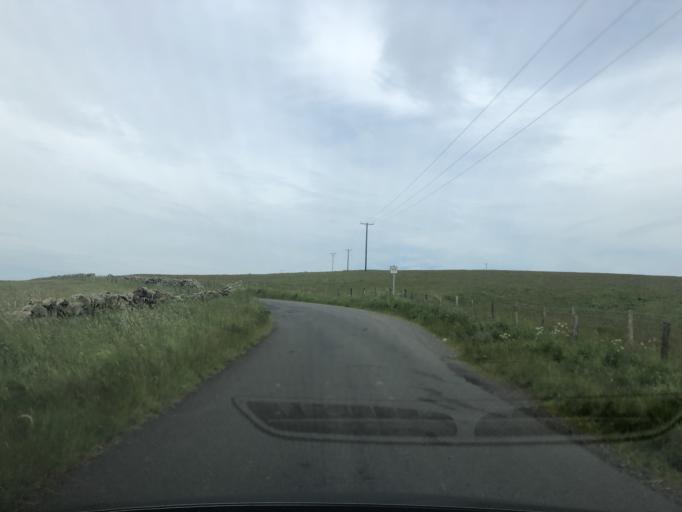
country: GB
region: Scotland
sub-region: The Scottish Borders
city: West Linton
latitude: 55.7652
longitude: -3.3243
